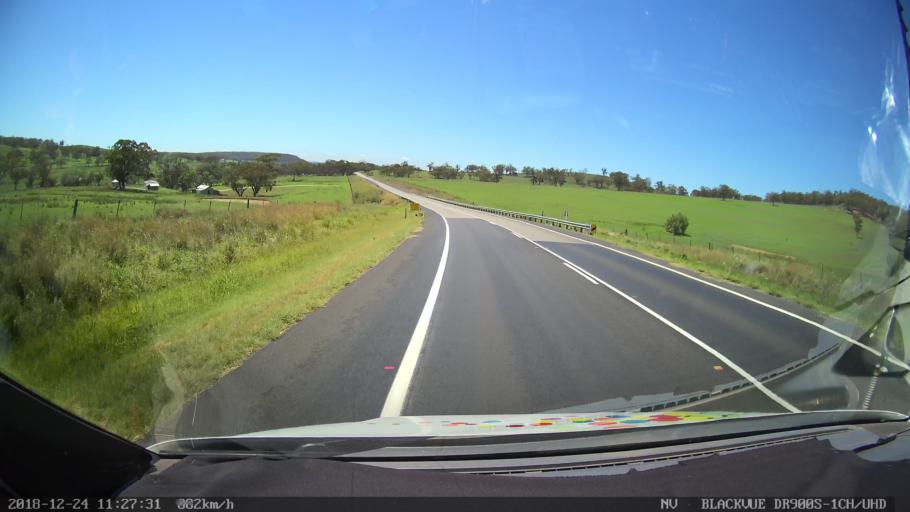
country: AU
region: New South Wales
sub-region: Upper Hunter Shire
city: Merriwa
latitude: -32.1828
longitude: 150.4357
